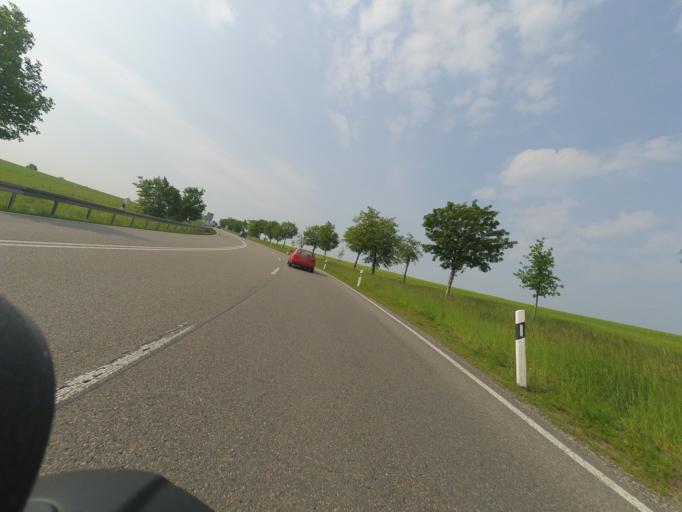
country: DE
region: Saxony
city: Bannewitz
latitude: 50.9607
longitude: 13.7026
